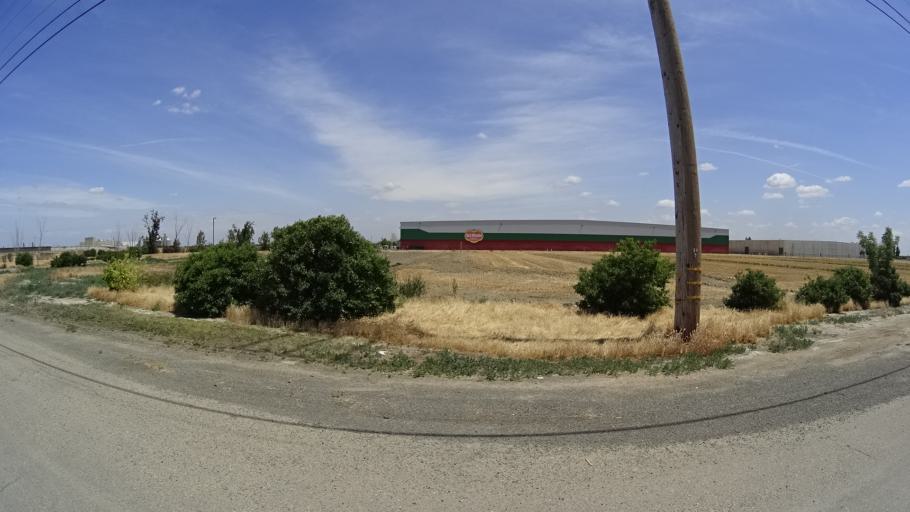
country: US
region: California
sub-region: Kings County
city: Home Garden
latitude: 36.2597
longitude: -119.6549
